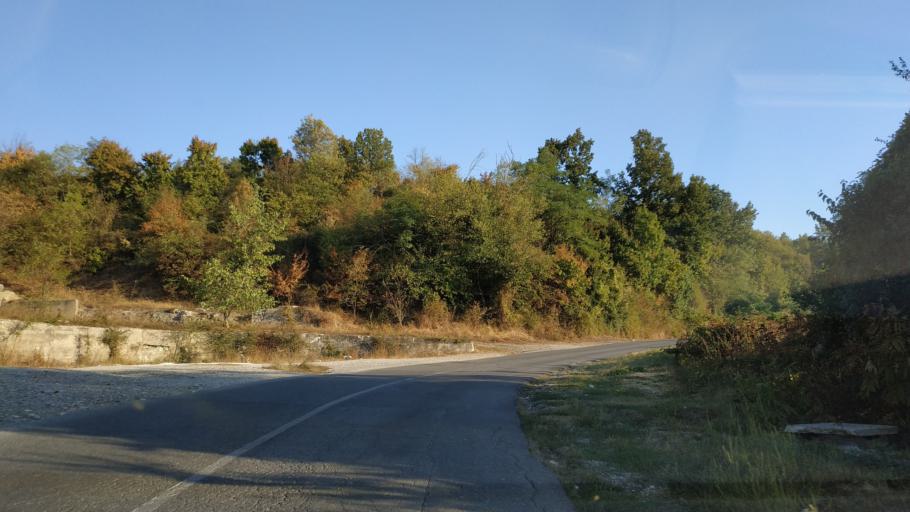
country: RS
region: Central Serbia
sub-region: Sumadijski Okrug
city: Topola
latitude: 44.2625
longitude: 20.6735
